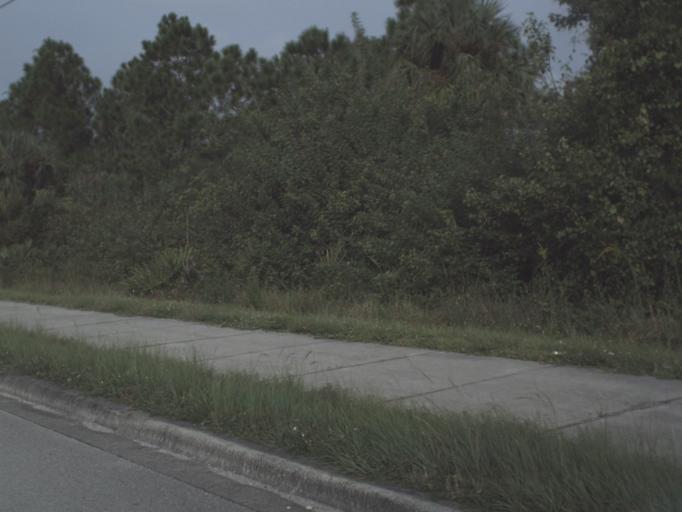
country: US
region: Florida
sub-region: Lee County
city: Suncoast Estates
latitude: 26.7147
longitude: -81.8322
